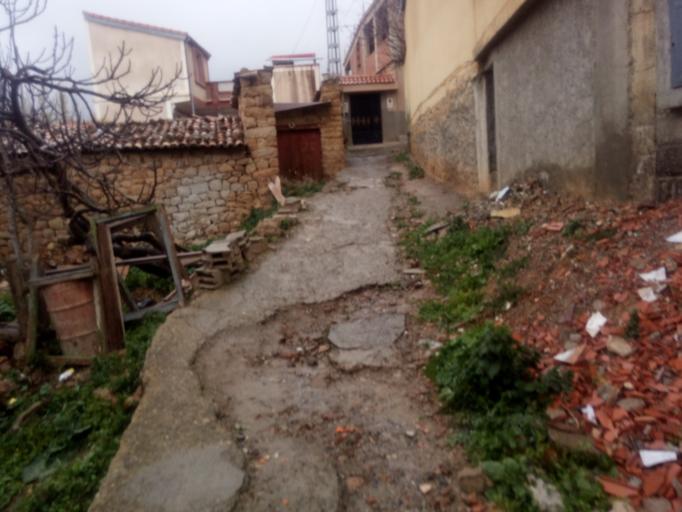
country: DZ
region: Tizi Ouzou
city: Chemini
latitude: 36.6019
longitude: 4.6358
